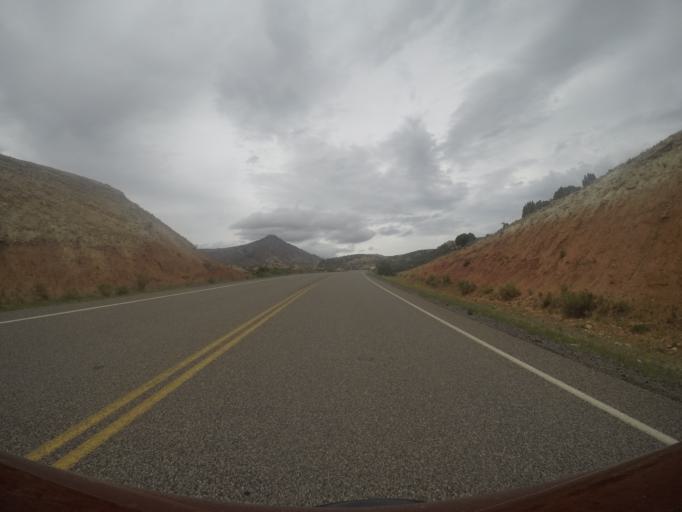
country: US
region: Wyoming
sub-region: Big Horn County
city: Lovell
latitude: 45.0054
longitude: -108.2685
